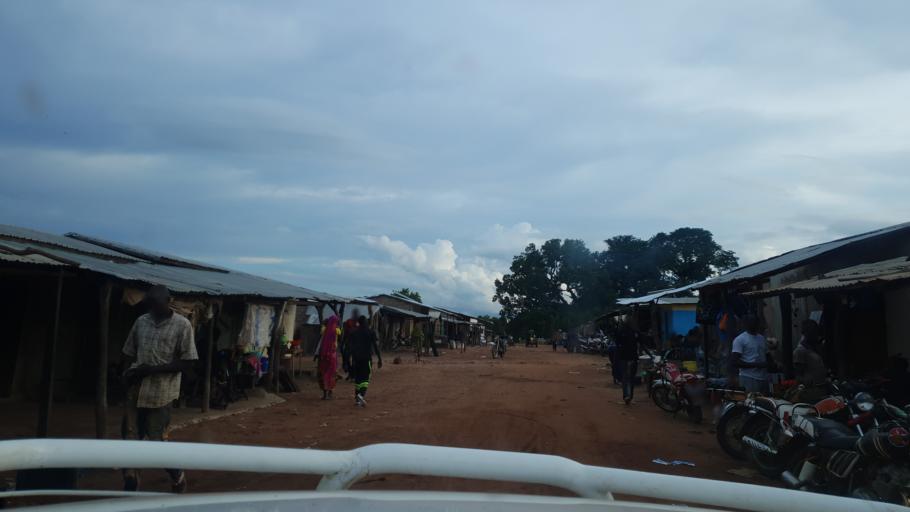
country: CI
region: Savanes
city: Tengrela
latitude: 10.5468
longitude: -6.9168
